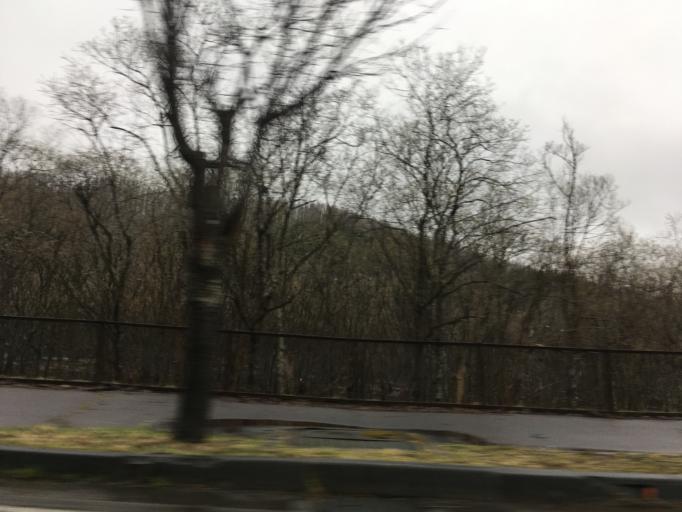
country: JP
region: Hokkaido
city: Nayoro
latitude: 44.0923
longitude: 142.4392
